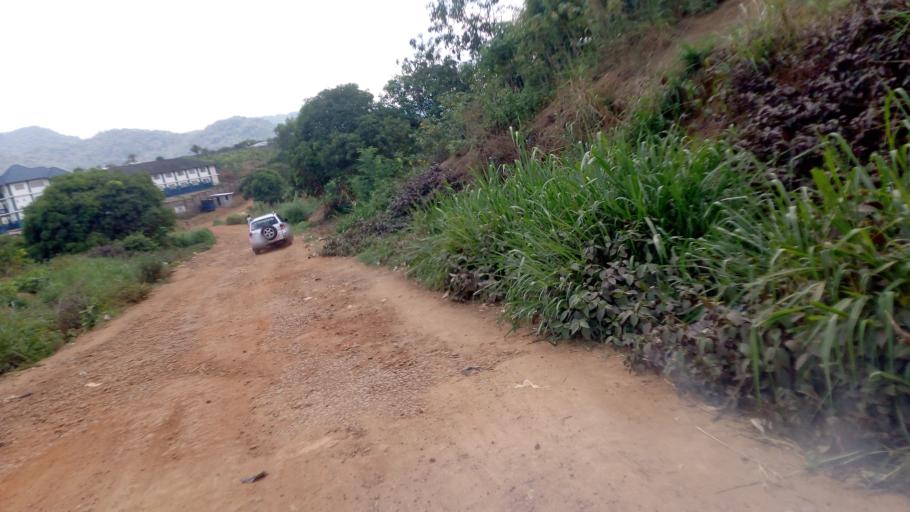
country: SL
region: Western Area
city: Waterloo
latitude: 8.3073
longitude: -13.0806
